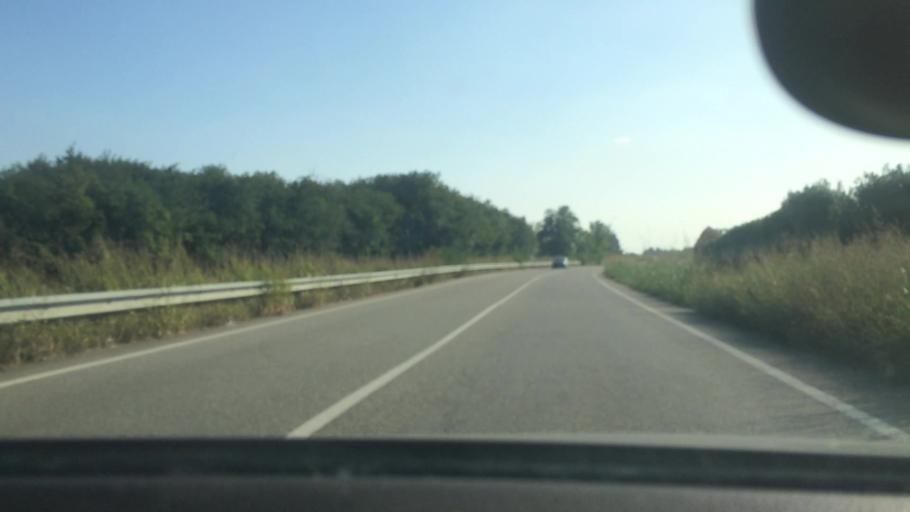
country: IT
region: Lombardy
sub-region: Citta metropolitana di Milano
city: Buscate
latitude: 45.5367
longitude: 8.8184
